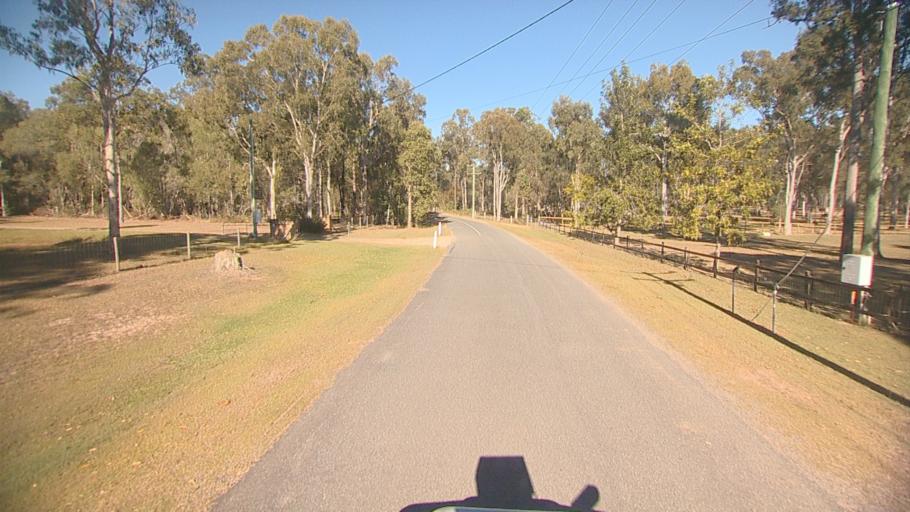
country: AU
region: Queensland
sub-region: Logan
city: Chambers Flat
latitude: -27.7904
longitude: 153.0661
